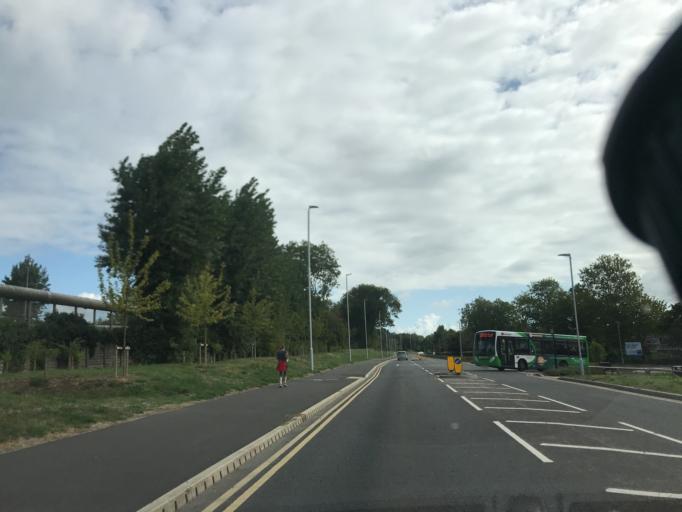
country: GB
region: England
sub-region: Buckinghamshire
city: Aylesbury
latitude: 51.8201
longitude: -0.7979
